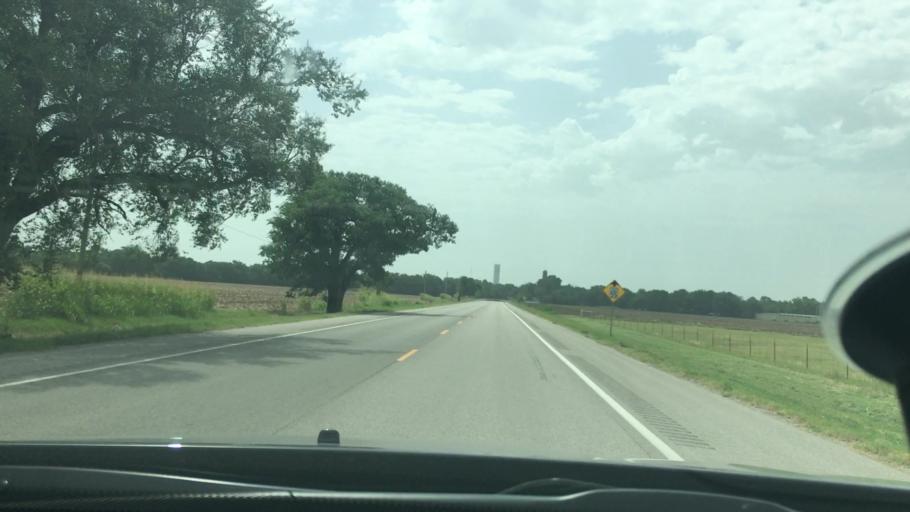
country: US
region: Oklahoma
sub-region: Garvin County
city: Pauls Valley
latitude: 34.8347
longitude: -97.2650
